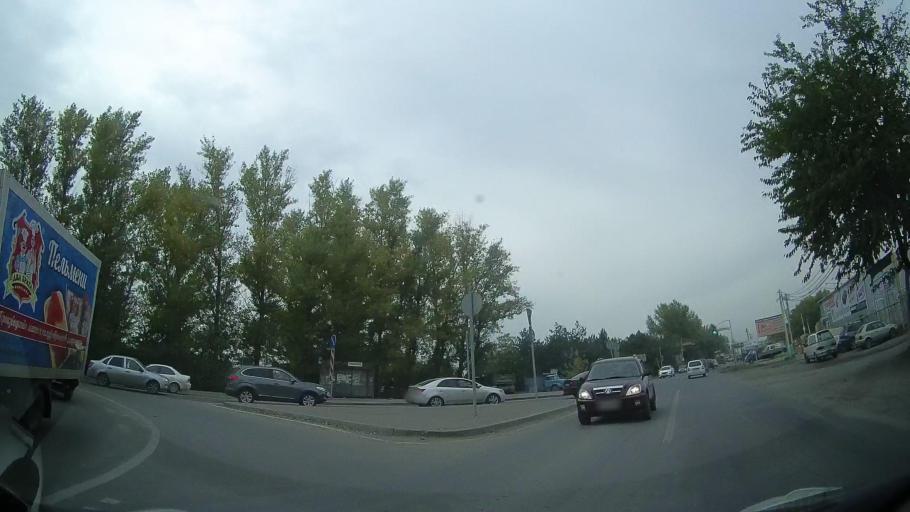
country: RU
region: Rostov
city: Severnyy
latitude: 47.2924
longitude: 39.6610
